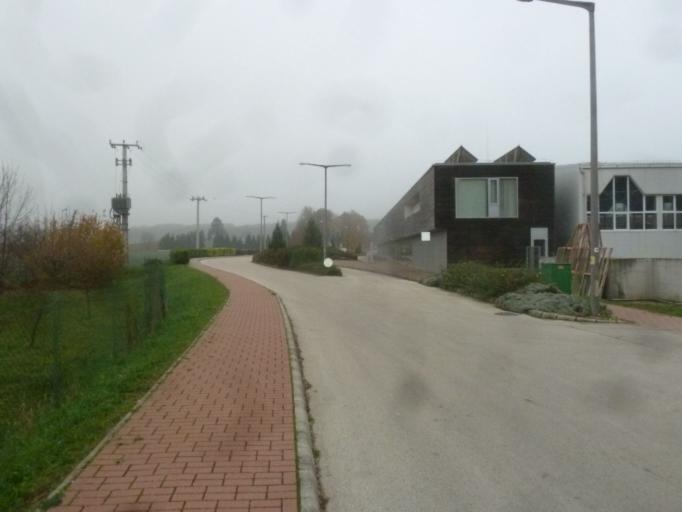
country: HU
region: Zala
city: Pacsa
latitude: 46.6024
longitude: 16.9904
